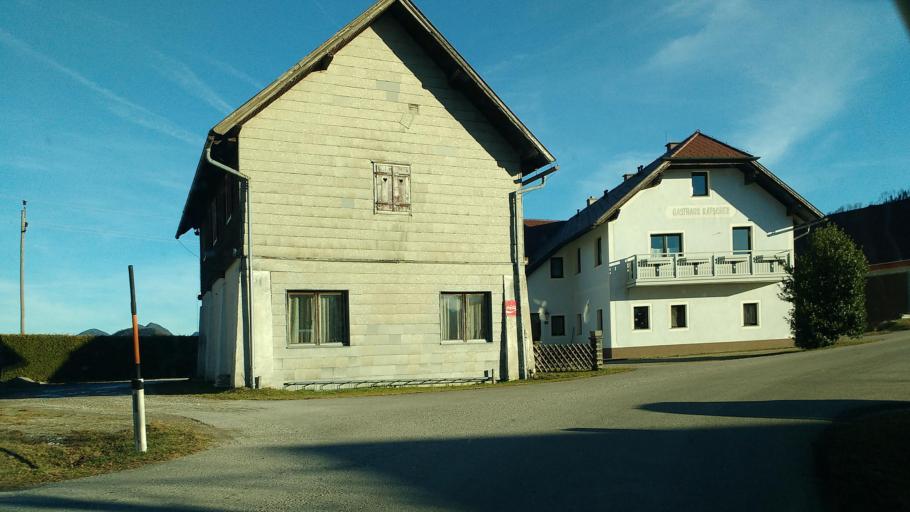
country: AT
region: Upper Austria
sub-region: Politischer Bezirk Kirchdorf an der Krems
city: Micheldorf in Oberoesterreich
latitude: 47.9040
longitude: 14.1604
